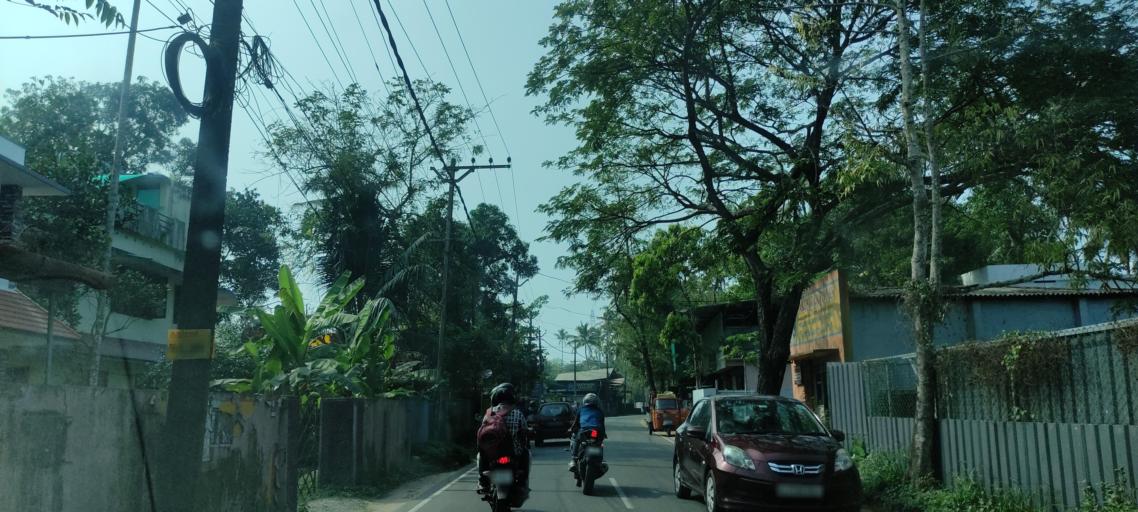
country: IN
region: Kerala
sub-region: Alappuzha
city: Vayalar
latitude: 9.6939
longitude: 76.3313
